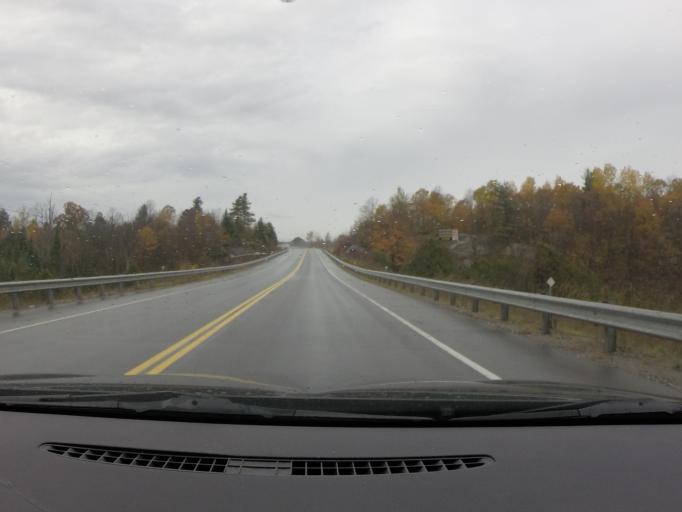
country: CA
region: Ontario
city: Perth
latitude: 44.8036
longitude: -76.6571
